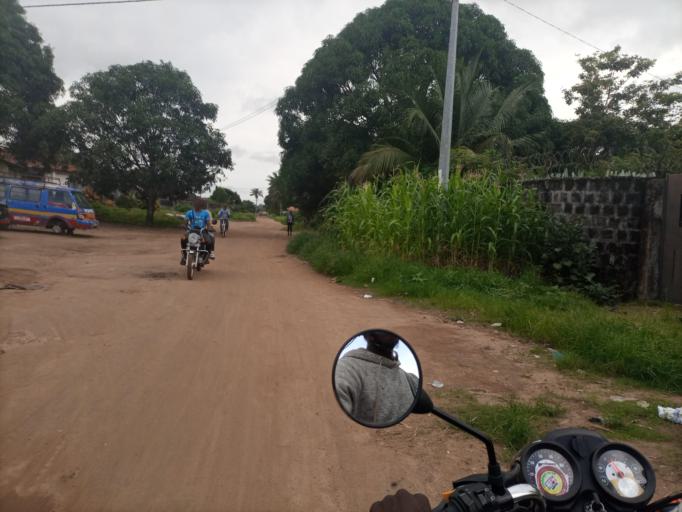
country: SL
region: Northern Province
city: Masoyila
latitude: 8.6048
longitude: -13.1755
